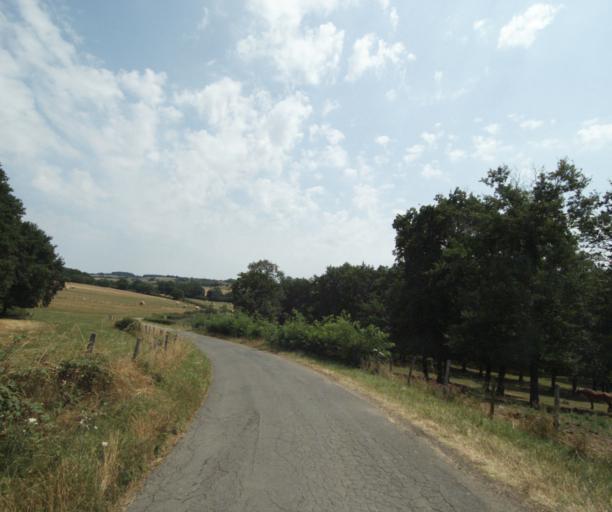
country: FR
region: Bourgogne
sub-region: Departement de Saone-et-Loire
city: Gueugnon
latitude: 46.5613
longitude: 4.0659
